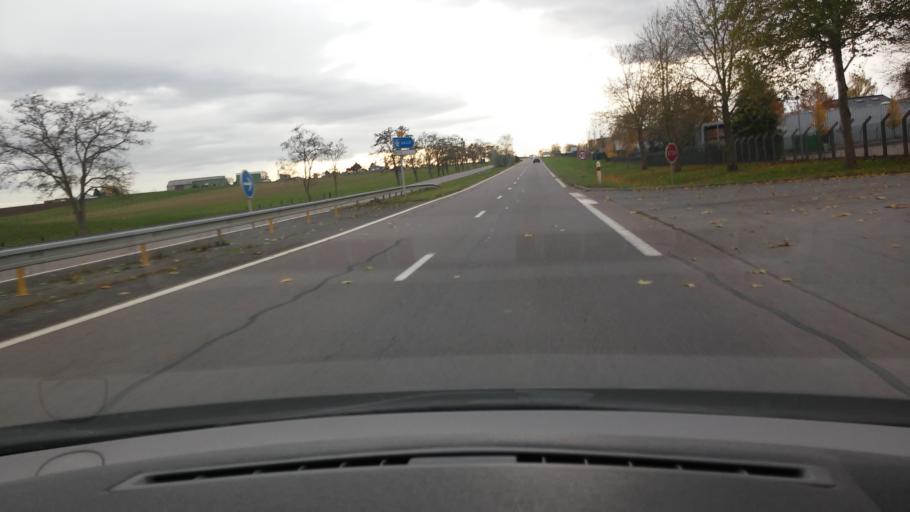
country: FR
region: Lorraine
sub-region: Departement de la Moselle
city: Ennery
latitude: 49.2150
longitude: 6.2100
